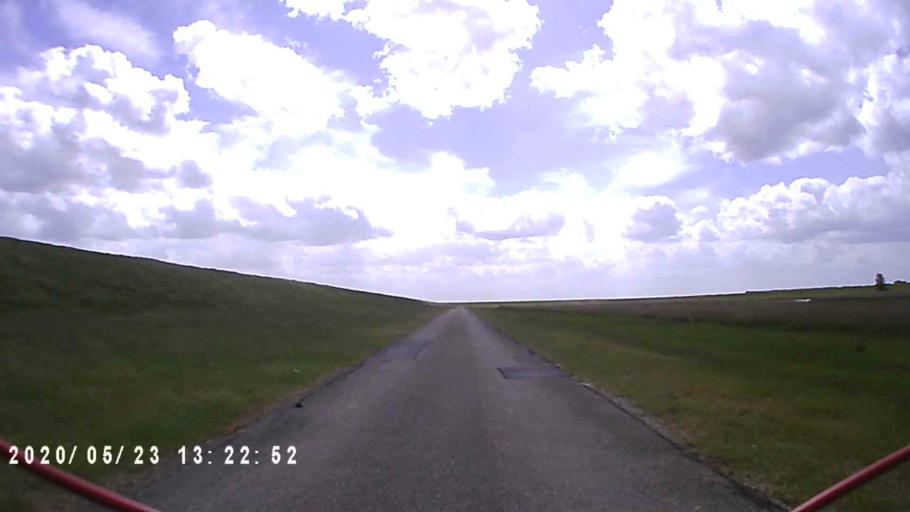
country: DE
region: Lower Saxony
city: Emden
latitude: 53.2894
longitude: 7.0816
